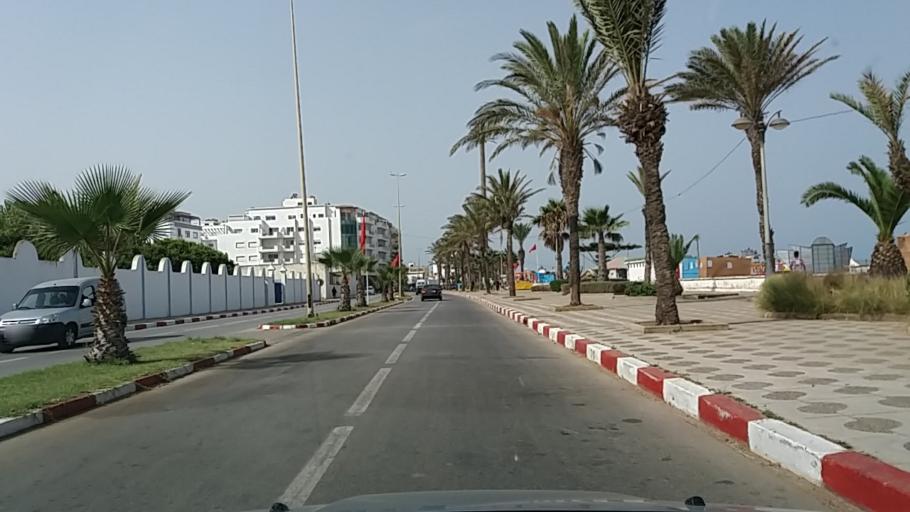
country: MA
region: Tanger-Tetouan
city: Asilah
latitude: 35.4727
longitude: -6.0290
